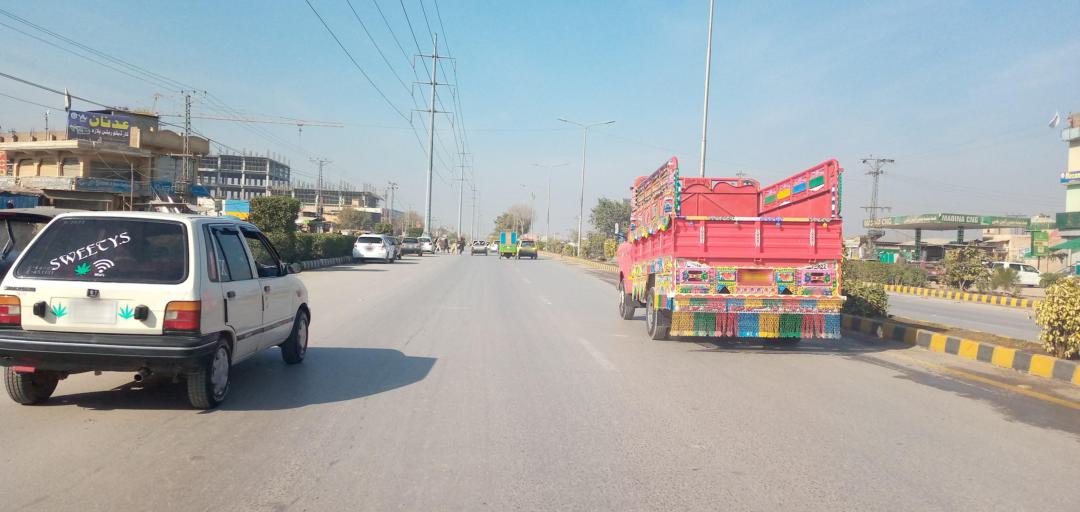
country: PK
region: Khyber Pakhtunkhwa
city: Peshawar
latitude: 33.9619
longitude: 71.5030
